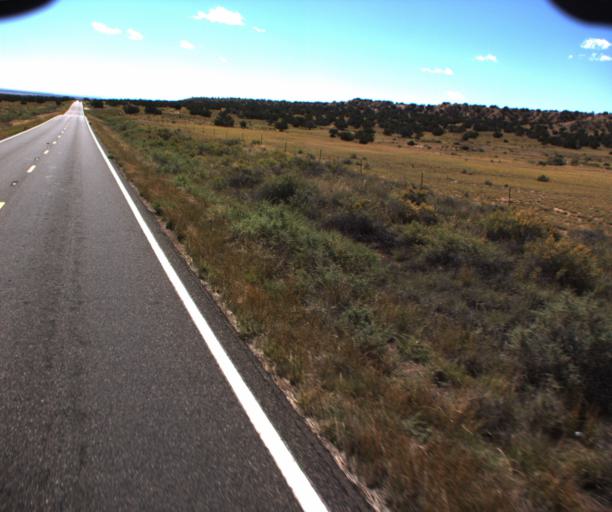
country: US
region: Arizona
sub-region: Apache County
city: Saint Johns
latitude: 34.7988
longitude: -109.2380
